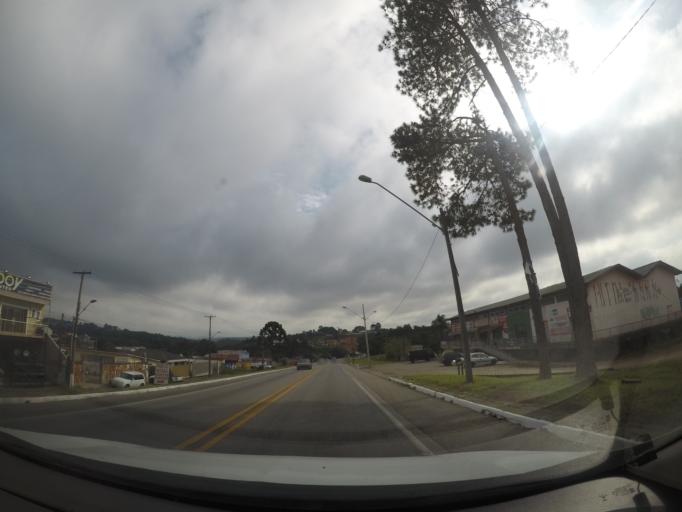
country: BR
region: Parana
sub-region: Colombo
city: Colombo
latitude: -25.3671
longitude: -49.2204
